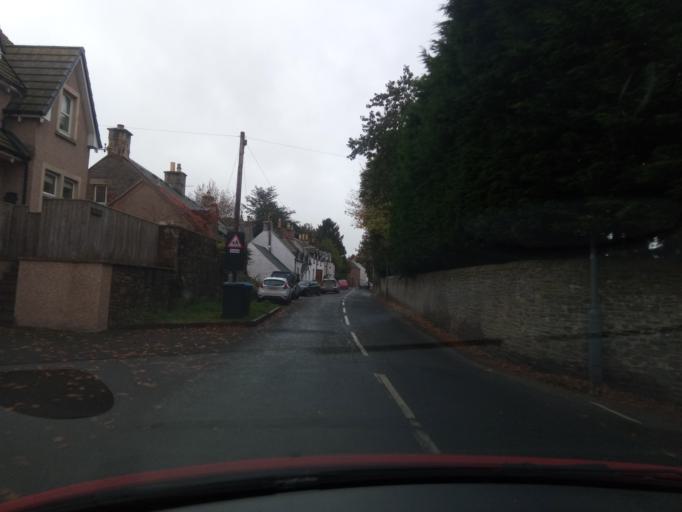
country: GB
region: Scotland
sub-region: The Scottish Borders
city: Melrose
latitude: 55.5189
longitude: -2.7355
